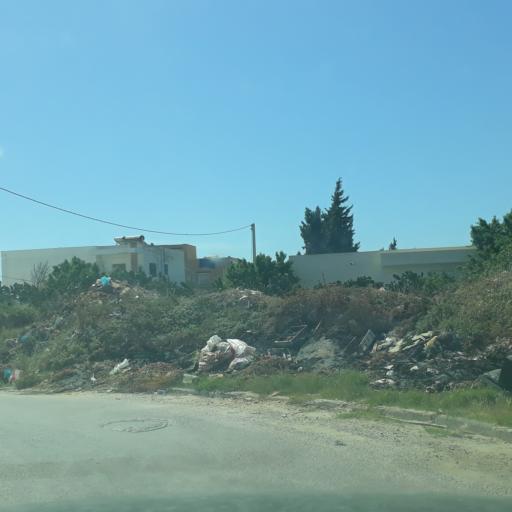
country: TN
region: Safaqis
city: Al Qarmadah
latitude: 34.7975
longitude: 10.7572
